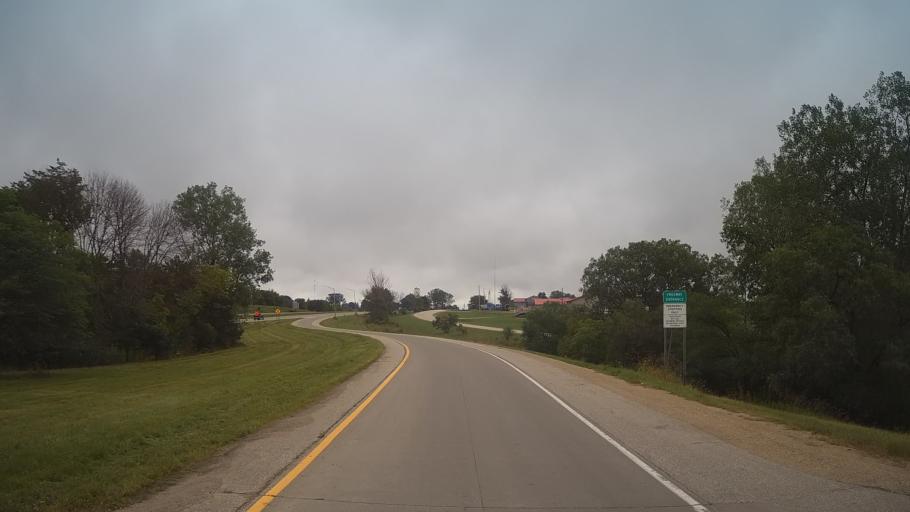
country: US
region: Minnesota
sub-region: Winona County
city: Winona
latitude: 43.9559
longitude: -91.6857
